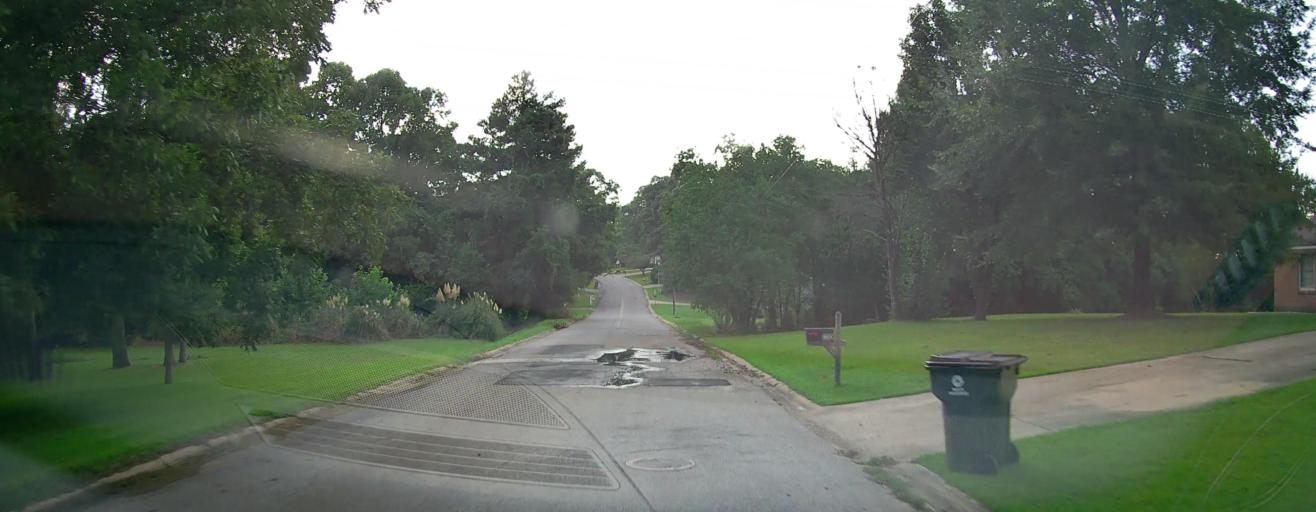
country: US
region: Georgia
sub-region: Houston County
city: Warner Robins
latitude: 32.5850
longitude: -83.6477
